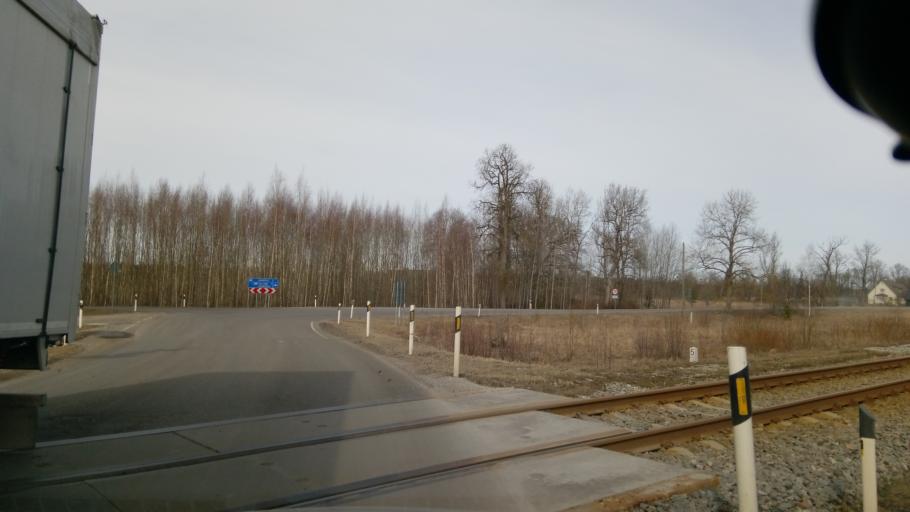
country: EE
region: Raplamaa
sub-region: Rapla vald
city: Rapla
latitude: 59.0188
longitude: 24.8376
